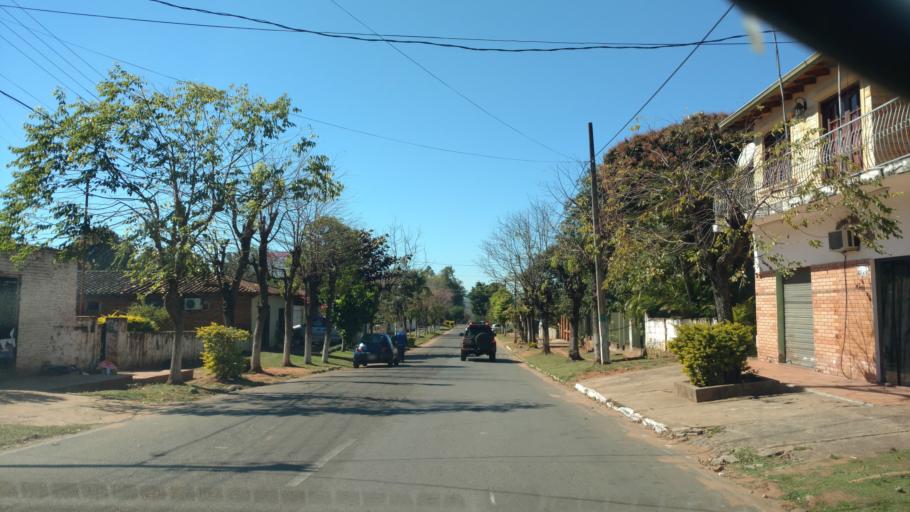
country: PY
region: Paraguari
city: Yaguaron
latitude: -25.5597
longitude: -57.2886
